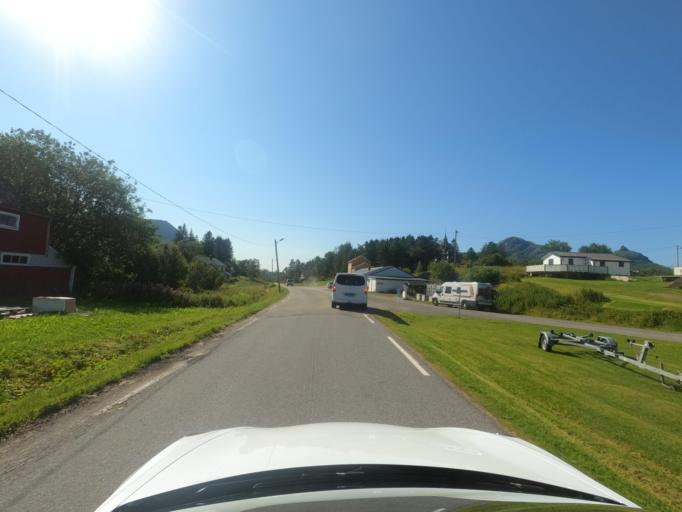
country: NO
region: Nordland
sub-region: Hadsel
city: Stokmarknes
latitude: 68.3134
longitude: 14.9875
